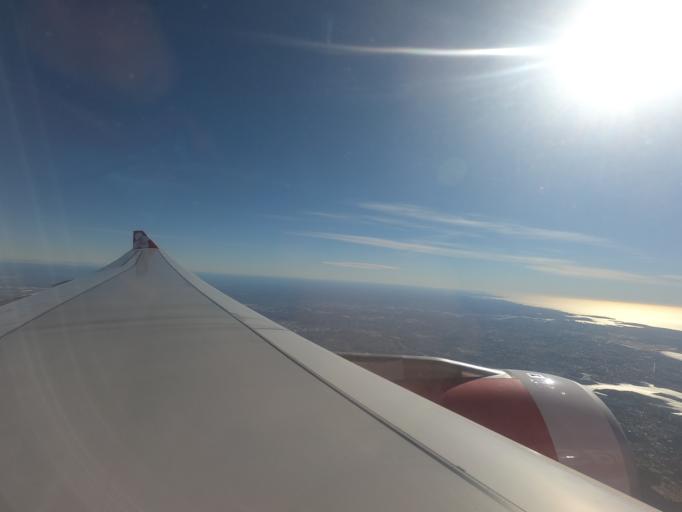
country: AU
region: New South Wales
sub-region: Sutherland Shire
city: Engadine
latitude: -34.0655
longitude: 151.0010
